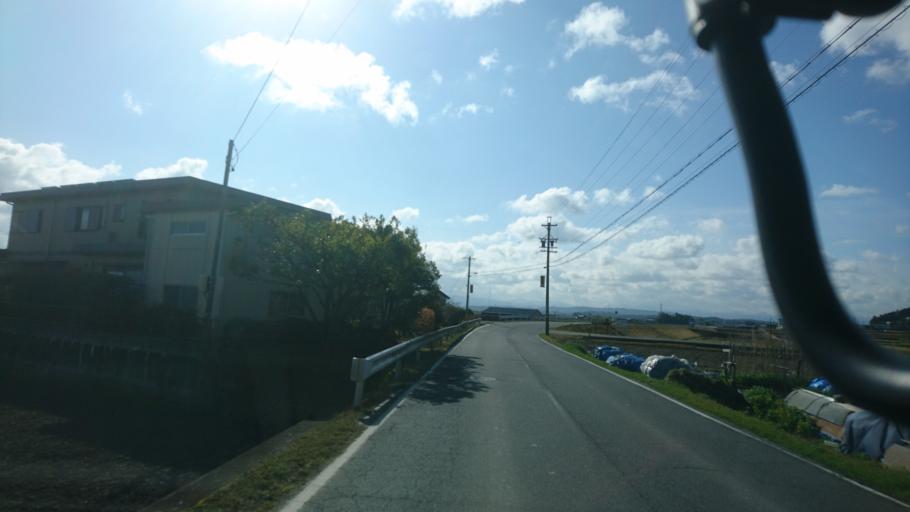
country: JP
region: Mie
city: Ueno-ebisumachi
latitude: 34.7653
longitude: 136.1088
